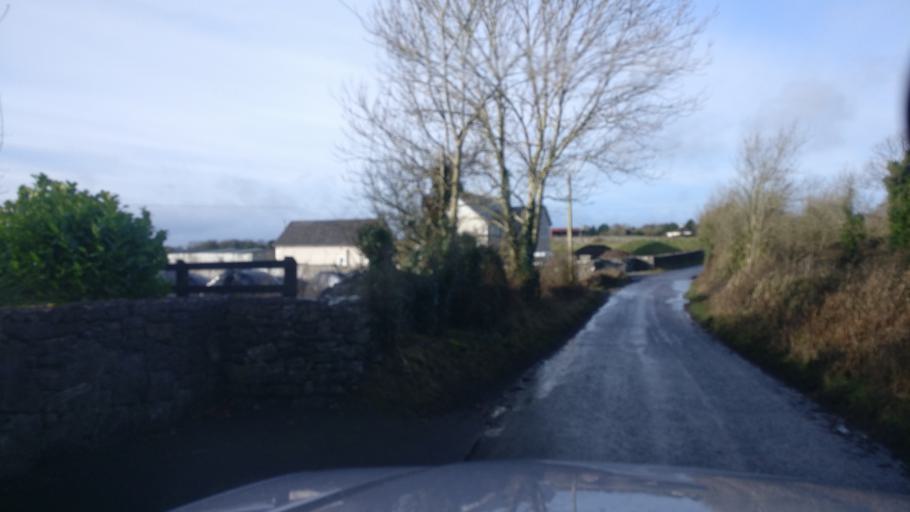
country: IE
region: Connaught
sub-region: County Galway
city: Loughrea
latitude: 53.1968
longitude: -8.6363
